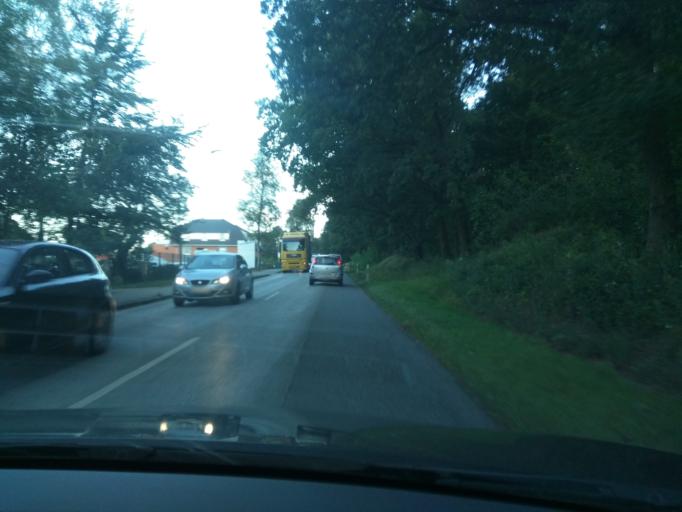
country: DE
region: Schleswig-Holstein
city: Kroppelshagen-Fahrendorf
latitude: 53.4554
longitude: 10.3479
